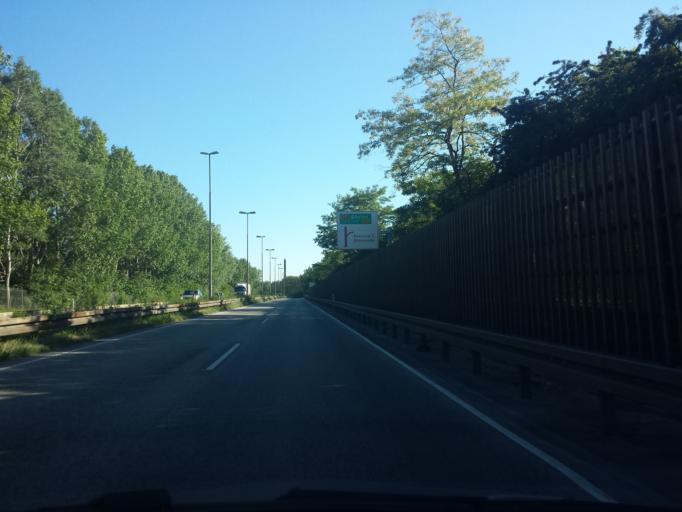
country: DK
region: Capital Region
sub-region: Ballerup Kommune
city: Ballerup
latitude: 55.7255
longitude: 12.3692
